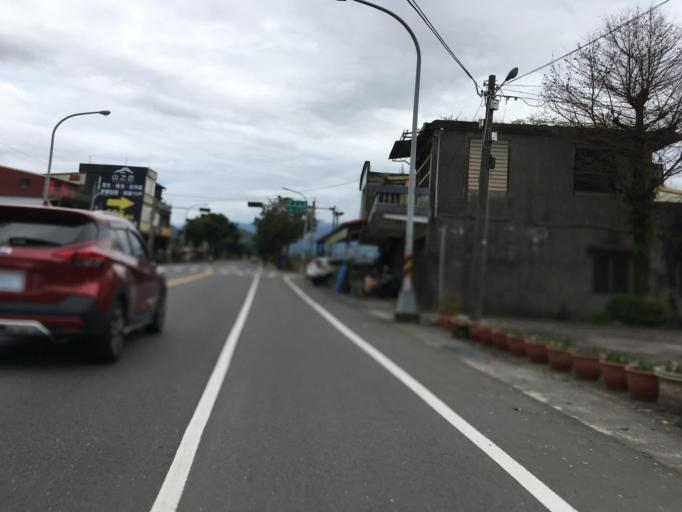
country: TW
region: Taiwan
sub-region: Yilan
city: Yilan
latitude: 24.6645
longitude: 121.6409
